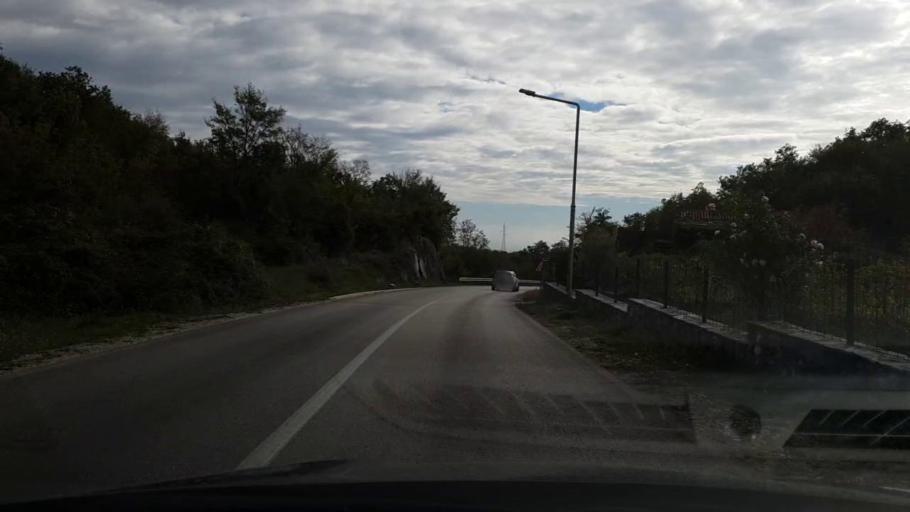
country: ME
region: Herceg Novi
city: Herceg-Novi
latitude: 42.4772
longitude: 18.5293
